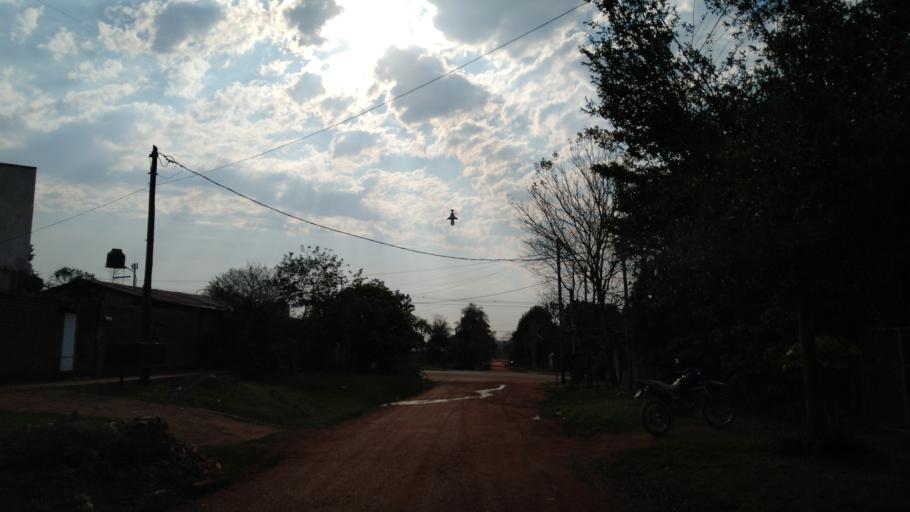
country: AR
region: Misiones
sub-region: Departamento de Capital
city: Posadas
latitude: -27.4276
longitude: -55.8777
